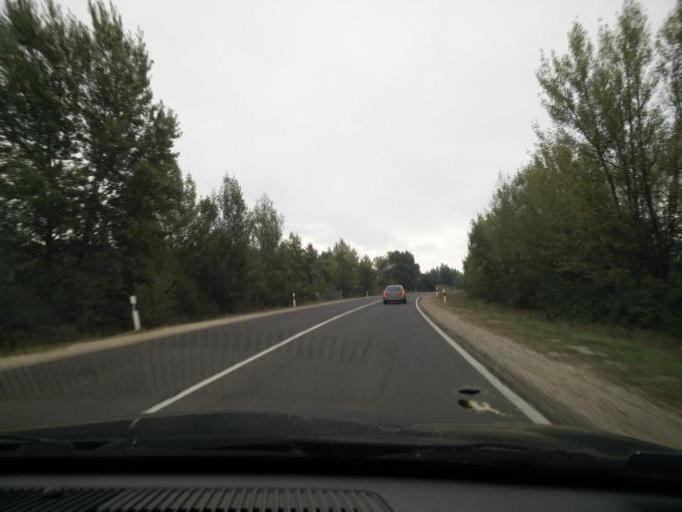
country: HU
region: Komarom-Esztergom
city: Dorog
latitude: 47.7356
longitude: 18.7543
